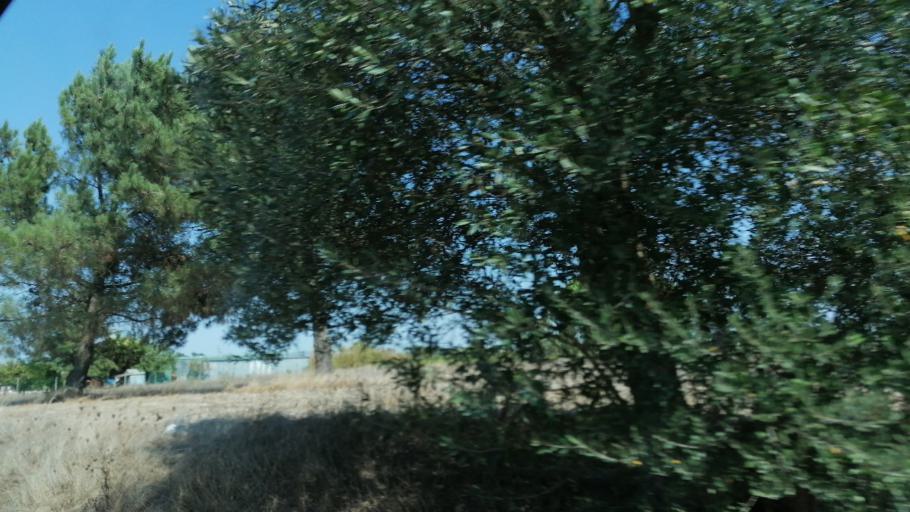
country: PT
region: Santarem
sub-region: Benavente
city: Poceirao
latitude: 38.6923
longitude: -8.7290
